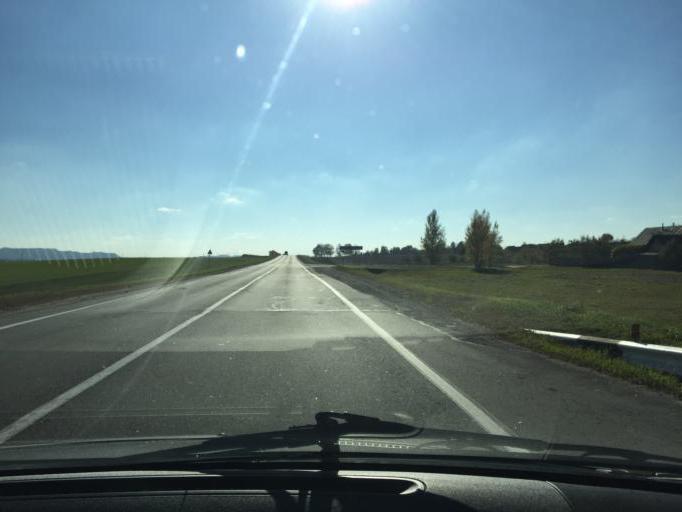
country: BY
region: Minsk
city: Slutsk
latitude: 52.9420
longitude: 27.4910
